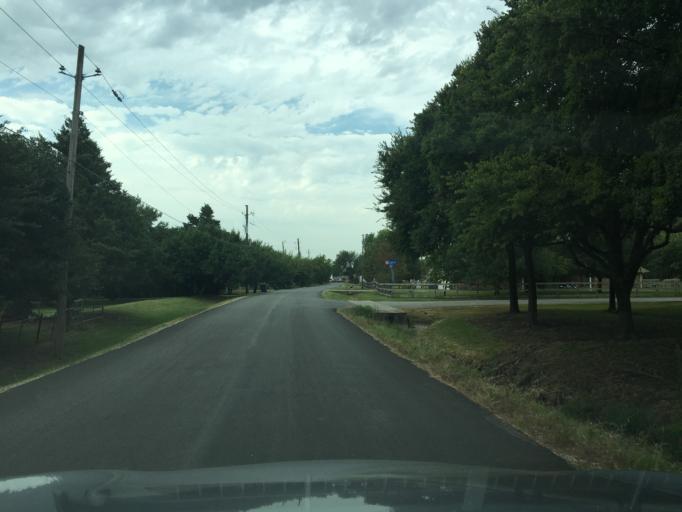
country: US
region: Texas
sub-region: Collin County
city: Parker
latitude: 33.0598
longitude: -96.6010
